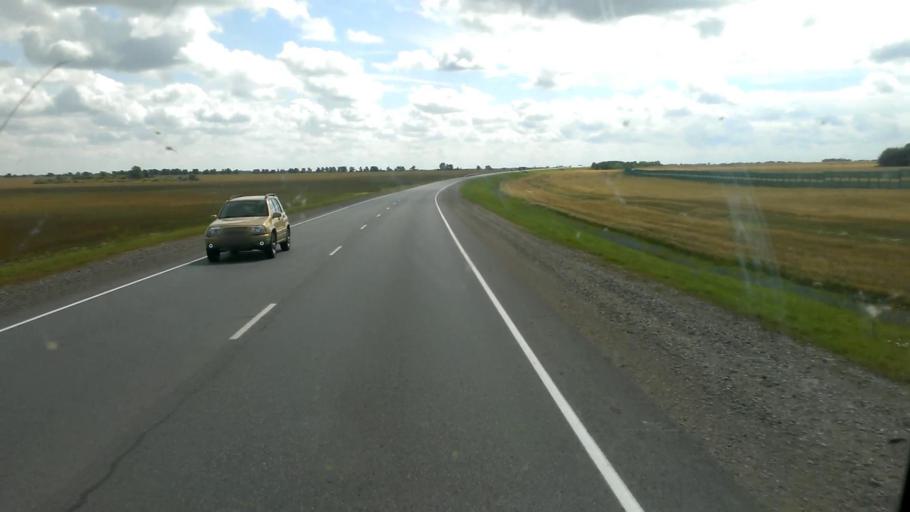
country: RU
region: Altai Krai
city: Troitskoye
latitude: 52.9141
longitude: 84.8192
